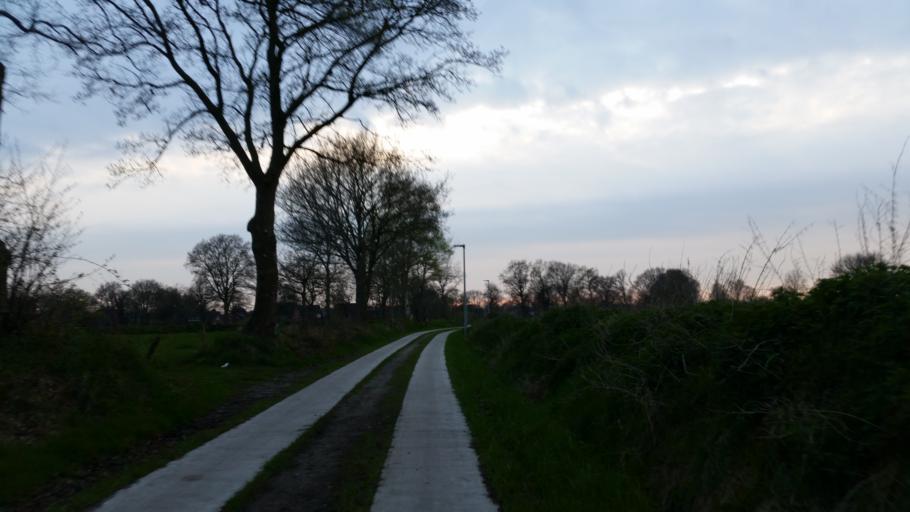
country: DE
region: Lower Saxony
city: Aurich
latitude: 53.4779
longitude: 7.4408
